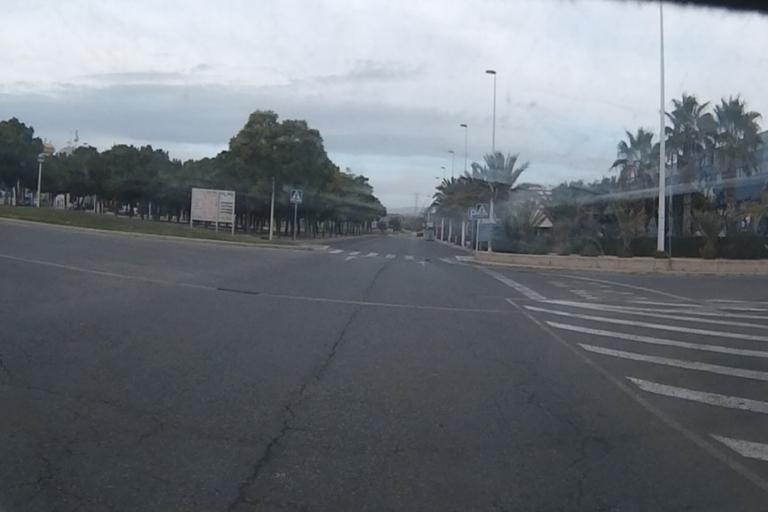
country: ES
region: Valencia
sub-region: Provincia de Alicante
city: Elche
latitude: 38.2923
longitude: -0.6107
